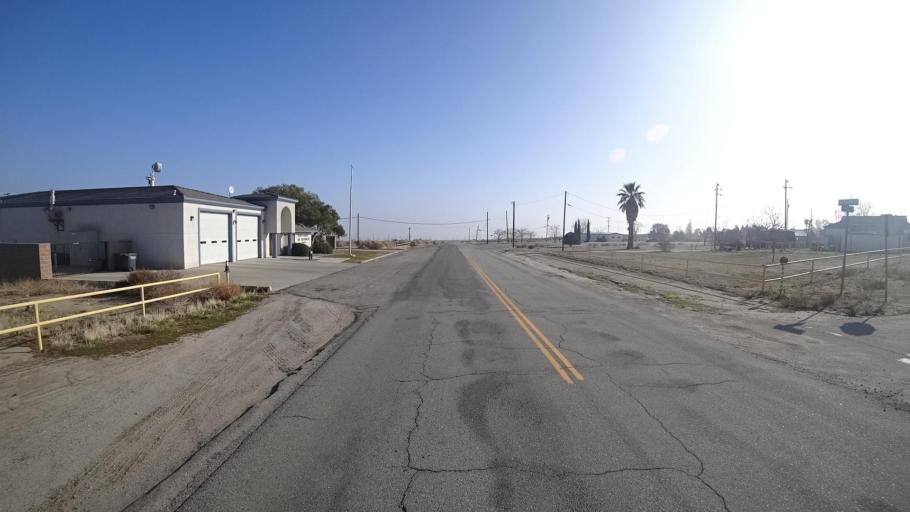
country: US
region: California
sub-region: Kern County
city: Taft Heights
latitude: 35.1795
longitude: -119.5427
